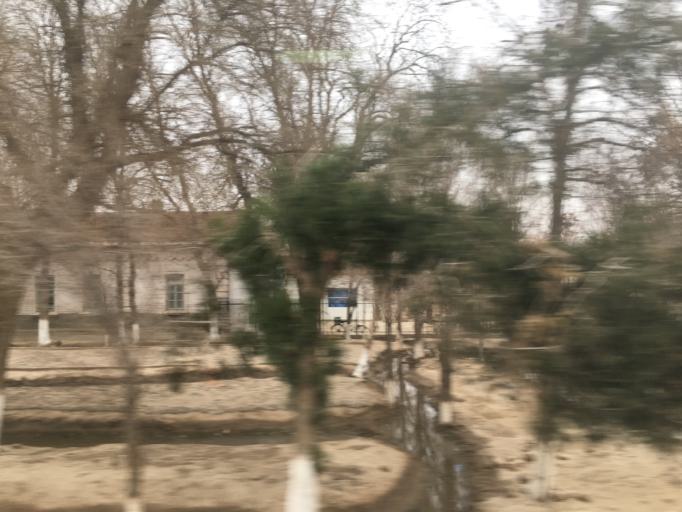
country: TM
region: Mary
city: Yoloeten
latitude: 36.5382
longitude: 62.5539
